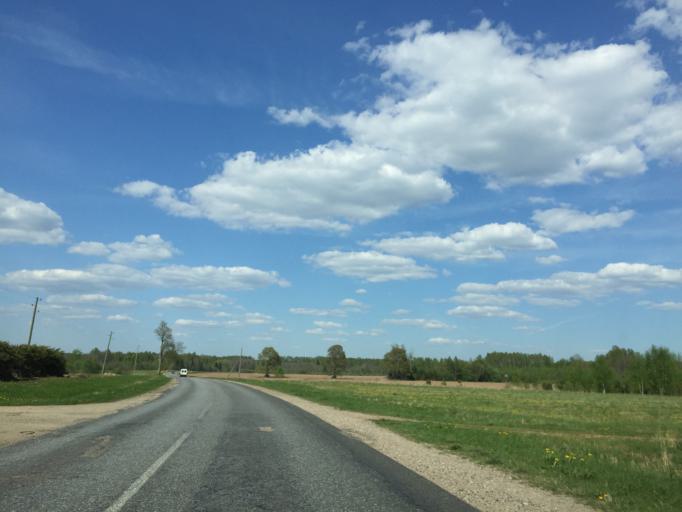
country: LV
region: Limbazu Rajons
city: Limbazi
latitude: 57.4313
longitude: 24.7143
